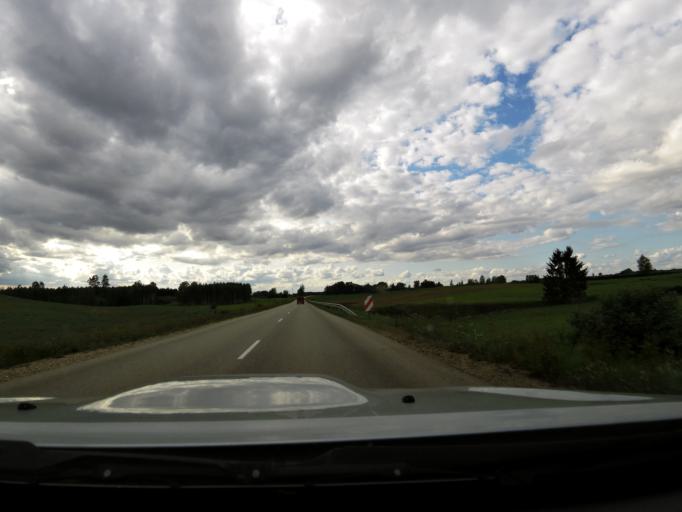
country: LV
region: Ilukste
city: Ilukste
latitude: 55.9829
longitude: 25.9960
